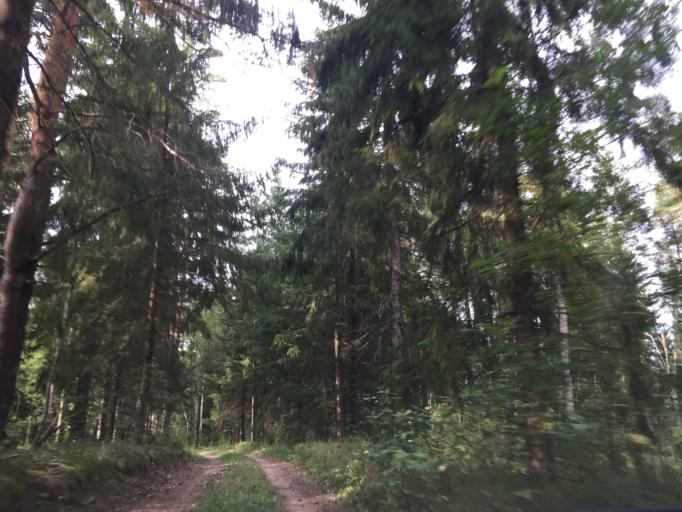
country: LV
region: Ikskile
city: Ikskile
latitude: 56.7622
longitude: 24.4697
